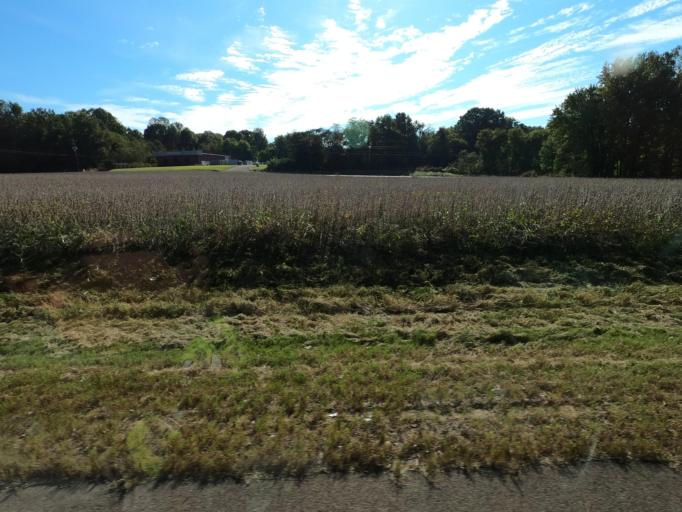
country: US
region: Tennessee
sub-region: Tipton County
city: Munford
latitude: 35.4311
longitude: -89.8074
